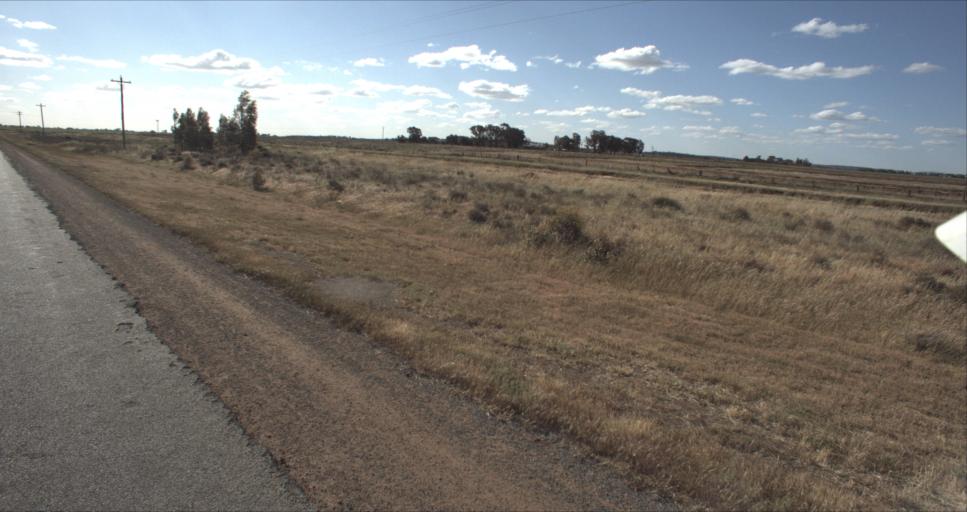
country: AU
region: New South Wales
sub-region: Leeton
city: Leeton
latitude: -34.4555
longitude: 146.2786
